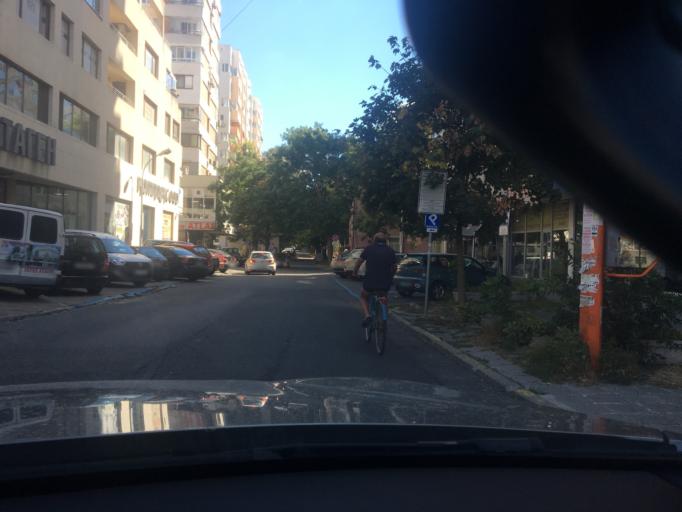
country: BG
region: Burgas
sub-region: Obshtina Burgas
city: Burgas
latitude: 42.5034
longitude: 27.4729
